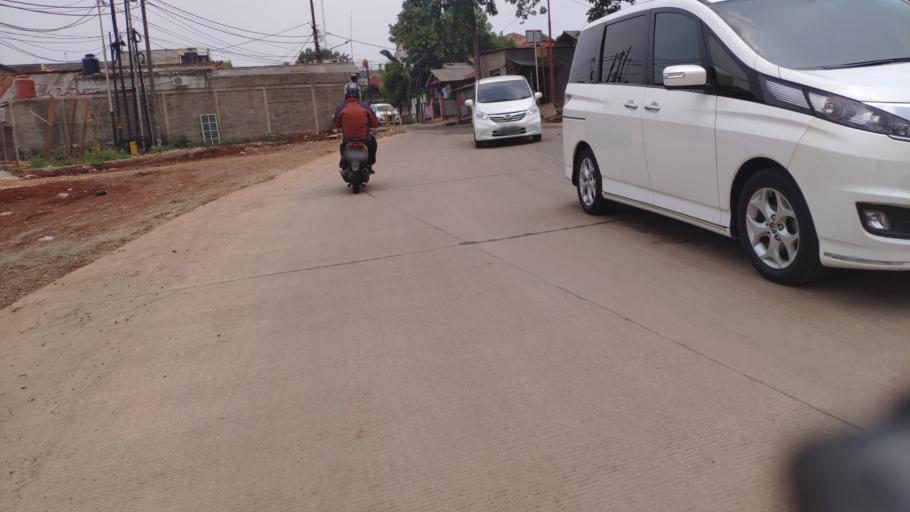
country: ID
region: West Java
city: Depok
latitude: -6.3437
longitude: 106.7998
